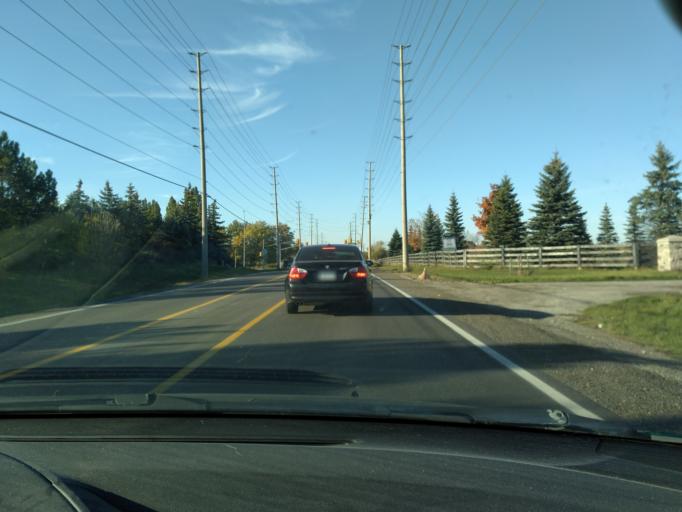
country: CA
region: Ontario
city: Brampton
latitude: 43.8751
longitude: -79.7111
